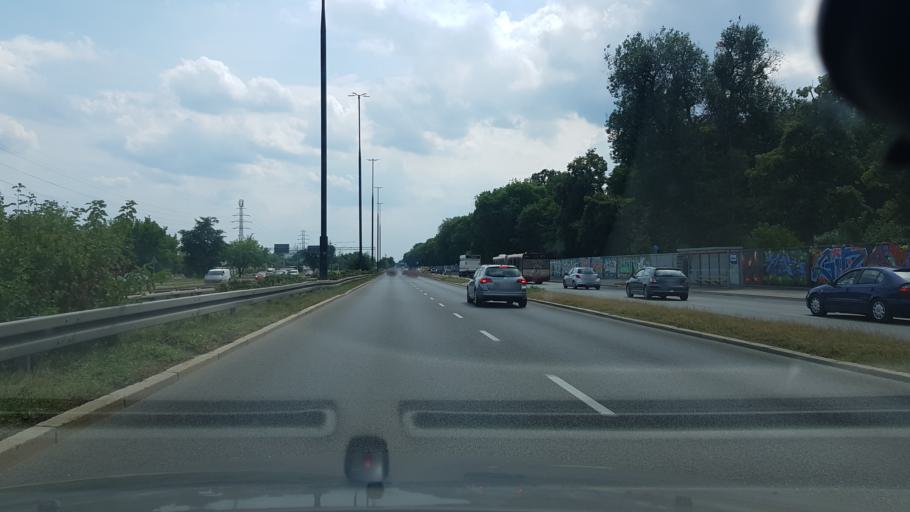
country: PL
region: Masovian Voivodeship
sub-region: Warszawa
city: Mokotow
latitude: 52.1648
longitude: 21.0174
